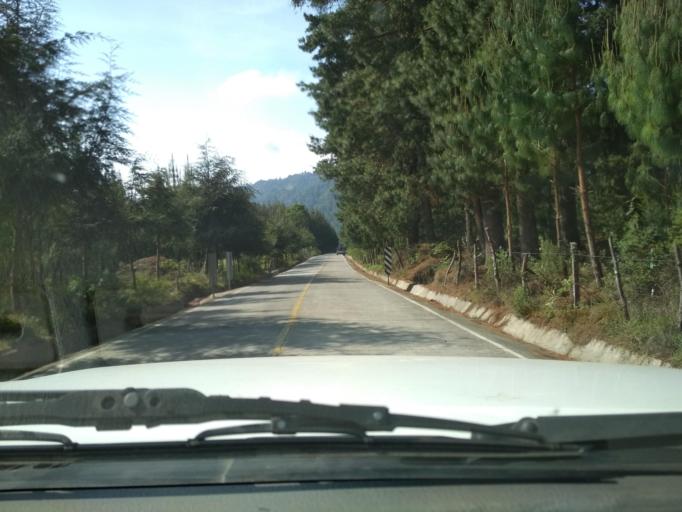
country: MX
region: Veracruz
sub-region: La Perla
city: Chilapa
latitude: 18.9958
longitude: -97.1862
